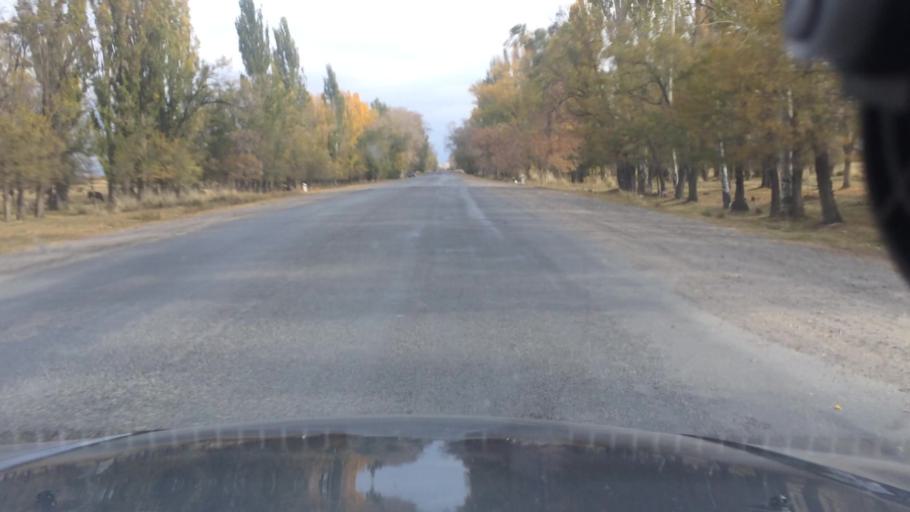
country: KG
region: Ysyk-Koel
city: Karakol
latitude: 42.5421
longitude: 78.3854
